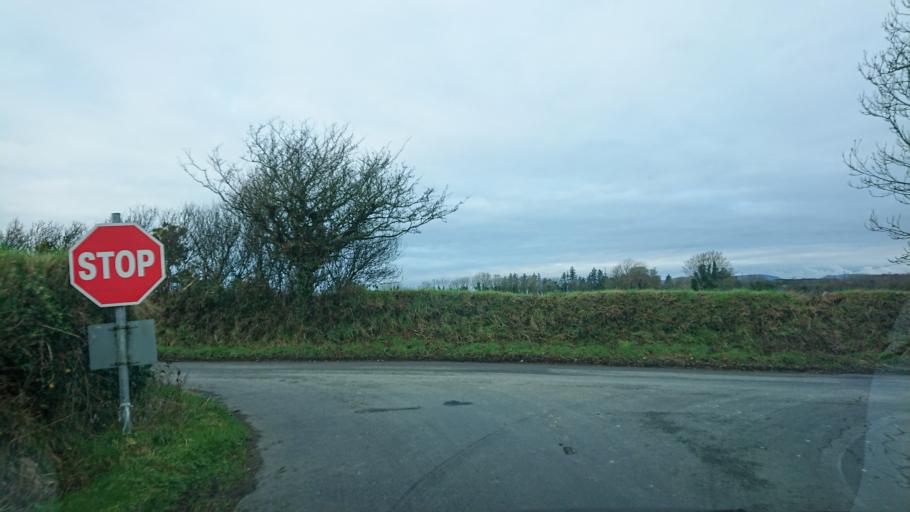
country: IE
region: Leinster
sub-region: Kilkenny
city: Mooncoin
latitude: 52.2240
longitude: -7.2730
